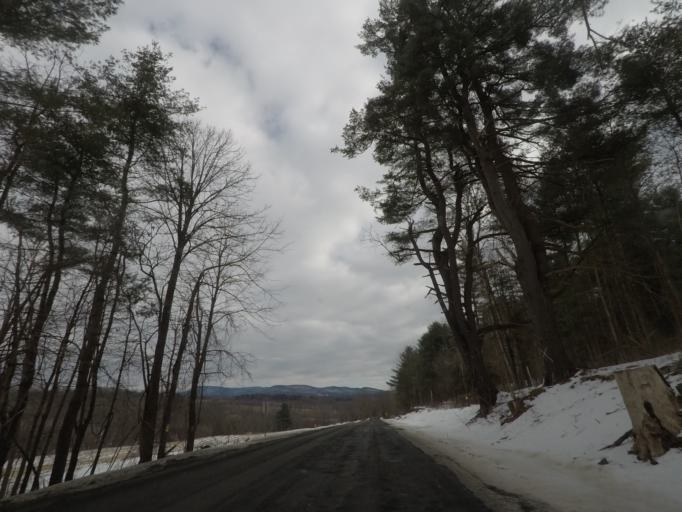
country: US
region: New York
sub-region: Rensselaer County
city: Hoosick Falls
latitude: 42.8630
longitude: -73.3611
